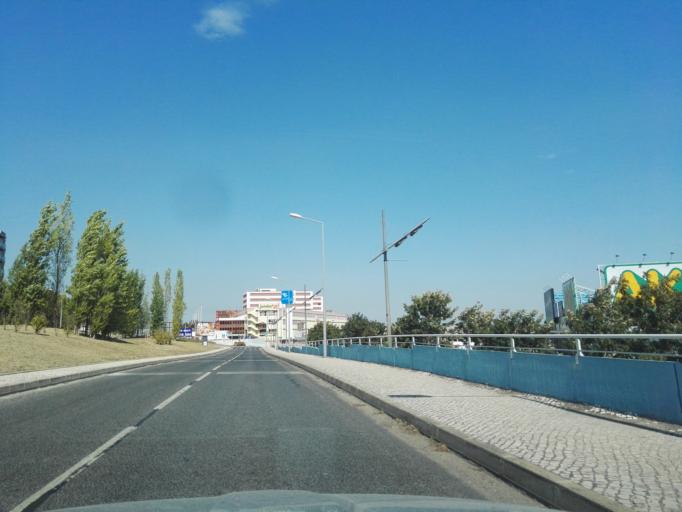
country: PT
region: Lisbon
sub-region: Vila Franca de Xira
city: Vialonga
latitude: 38.8859
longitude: -9.0471
